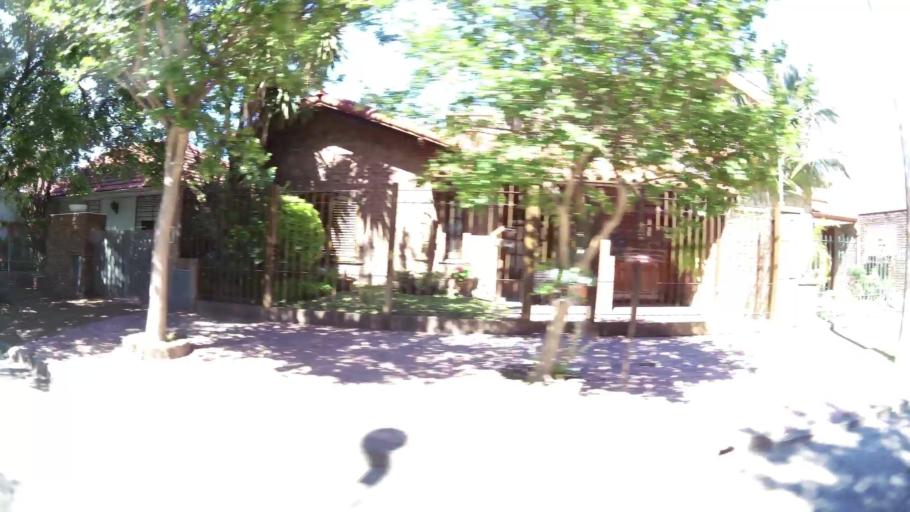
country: AR
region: Buenos Aires
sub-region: Partido de General San Martin
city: General San Martin
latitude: -34.5246
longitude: -58.5342
